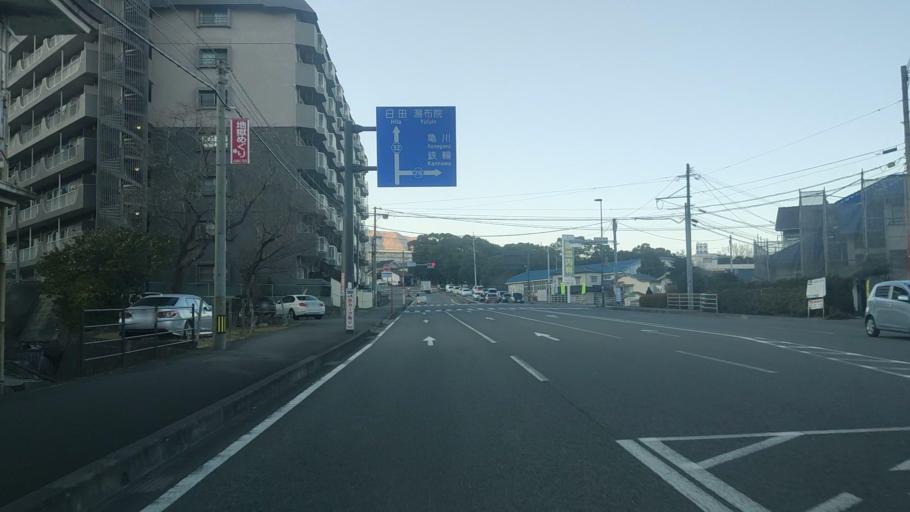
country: JP
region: Oita
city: Beppu
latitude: 33.2872
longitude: 131.4734
